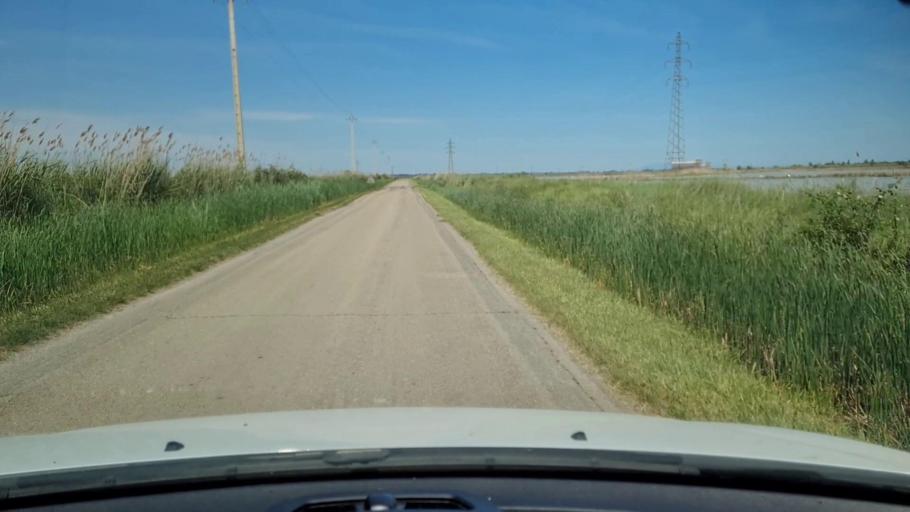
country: FR
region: Languedoc-Roussillon
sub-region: Departement du Gard
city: Saint-Gilles
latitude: 43.5757
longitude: 4.3968
